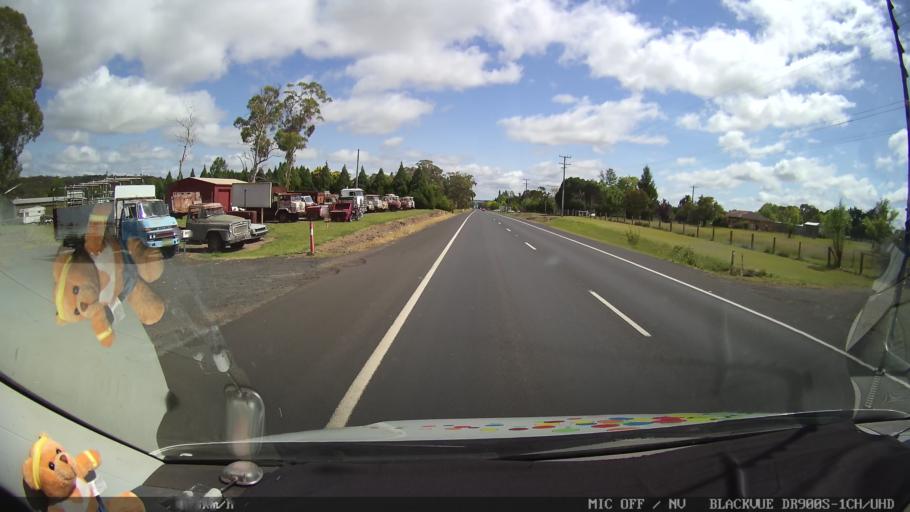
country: AU
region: New South Wales
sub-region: Glen Innes Severn
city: Glen Innes
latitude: -29.7642
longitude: 151.7333
